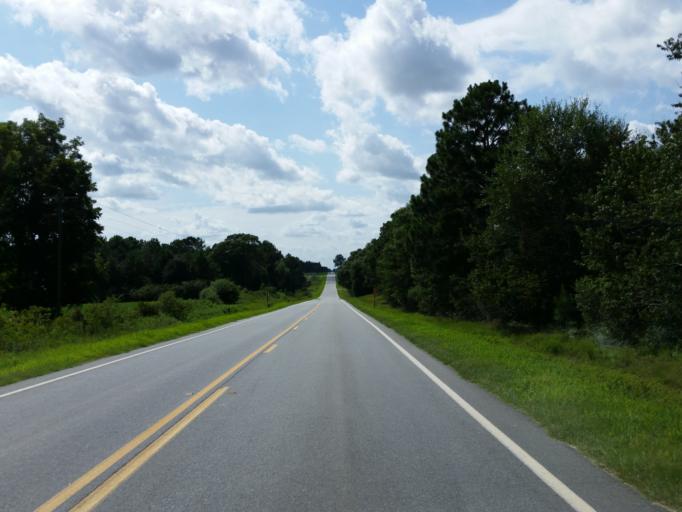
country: US
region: Georgia
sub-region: Turner County
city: Ashburn
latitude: 31.6365
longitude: -83.5173
